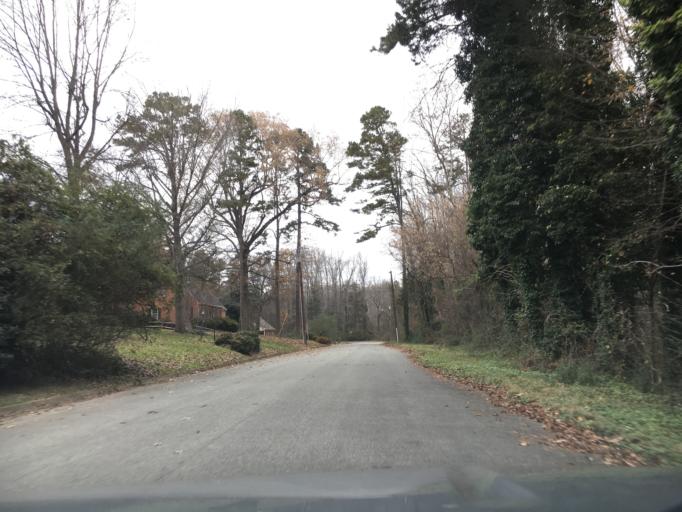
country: US
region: Virginia
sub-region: Halifax County
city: South Boston
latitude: 36.7087
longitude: -78.8923
